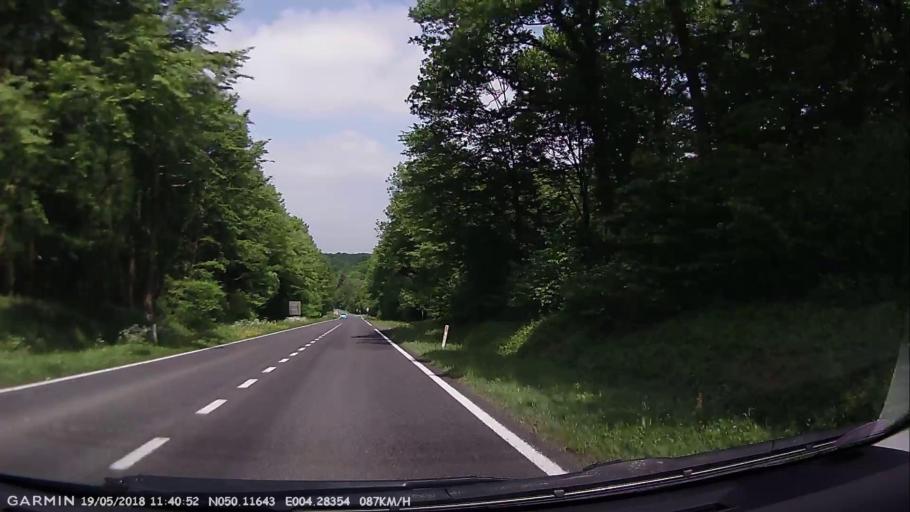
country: BE
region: Wallonia
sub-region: Province du Hainaut
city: Froidchapelle
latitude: 50.1167
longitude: 4.2835
